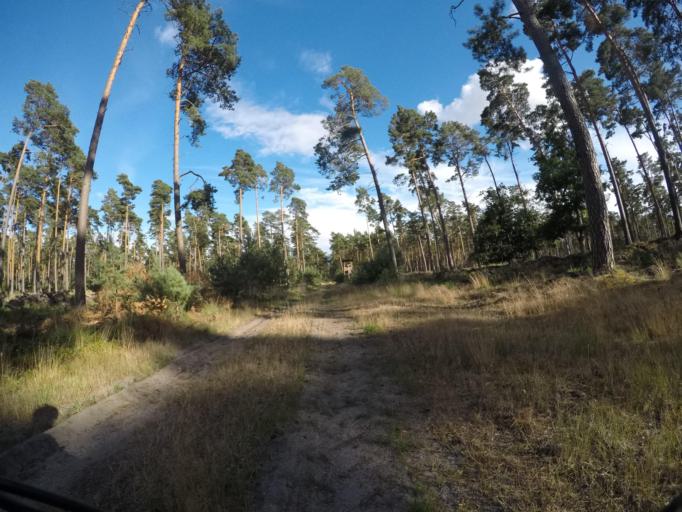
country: DE
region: Mecklenburg-Vorpommern
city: Lubtheen
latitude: 53.2559
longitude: 10.9969
